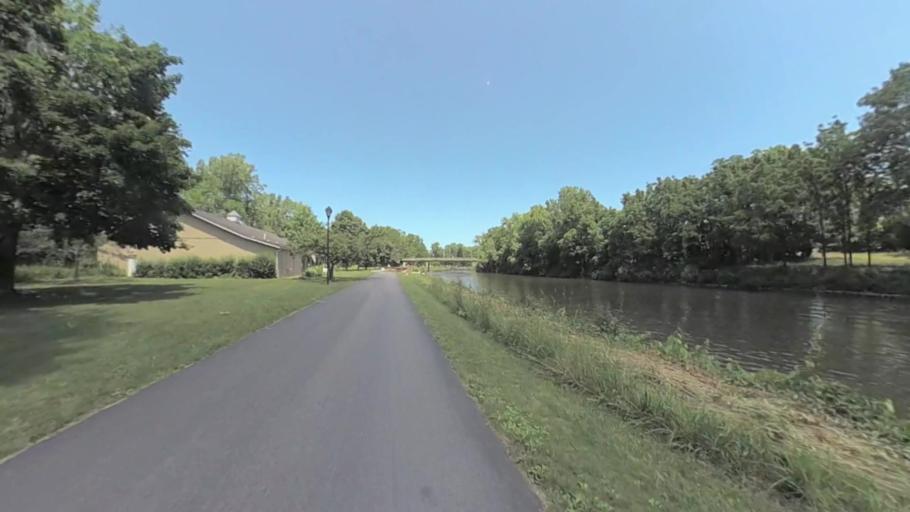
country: US
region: New York
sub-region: Monroe County
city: Fairport
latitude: 43.0987
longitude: -77.4562
